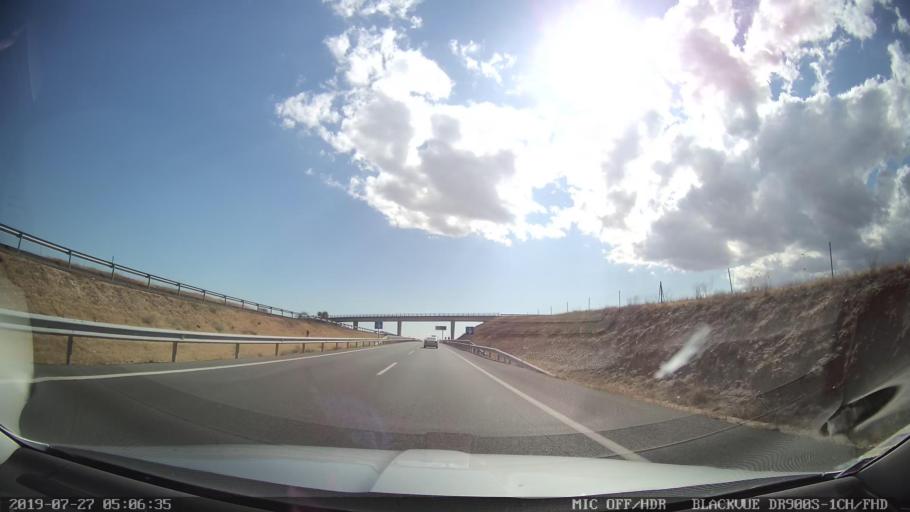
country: ES
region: Castille-La Mancha
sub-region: Province of Toledo
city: Santa Cruz del Retamar
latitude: 40.1294
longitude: -4.2147
